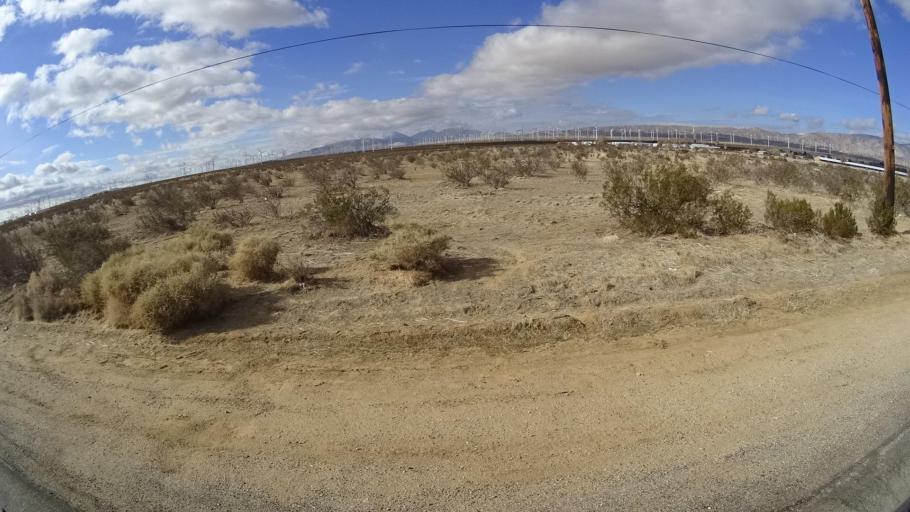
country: US
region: California
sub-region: Kern County
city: Mojave
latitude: 35.0454
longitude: -118.1848
